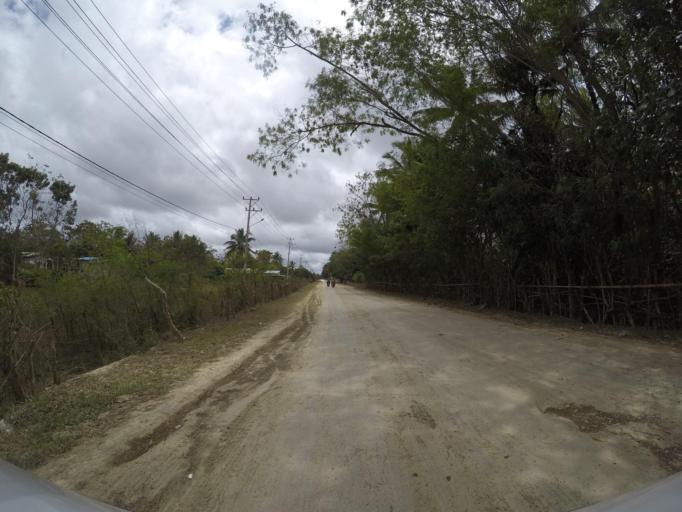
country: TL
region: Lautem
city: Lospalos
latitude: -8.4756
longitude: 126.9927
